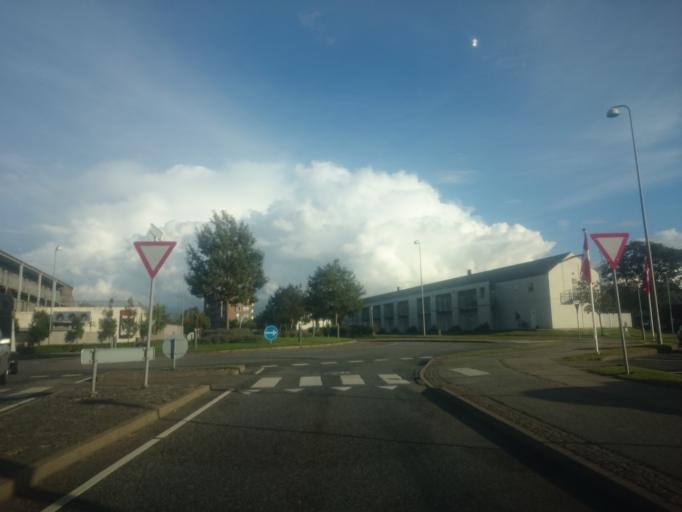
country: DK
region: South Denmark
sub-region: Billund Kommune
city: Billund
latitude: 55.7300
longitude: 9.1138
